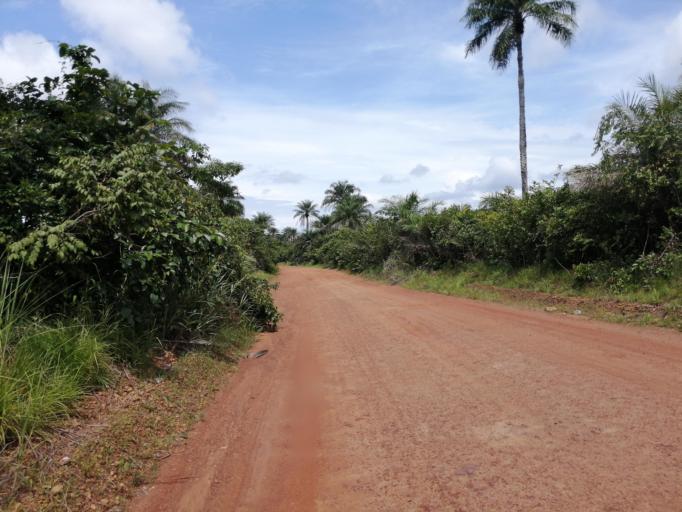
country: SL
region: Northern Province
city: Pepel
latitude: 8.6479
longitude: -13.0153
